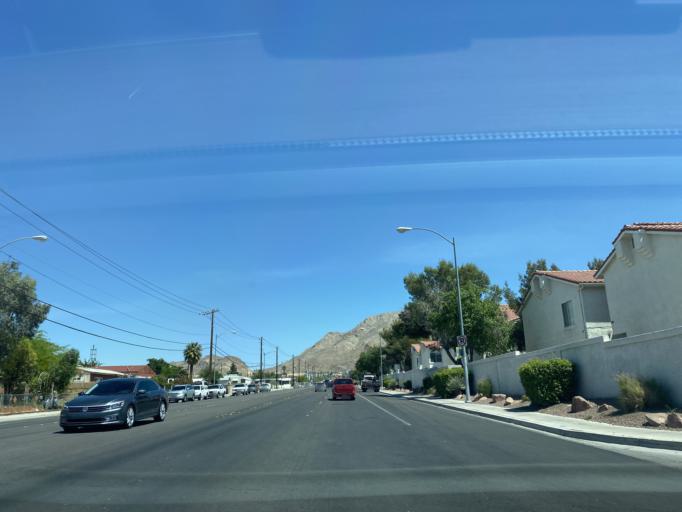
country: US
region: Nevada
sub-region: Clark County
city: Sunrise Manor
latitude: 36.1960
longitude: -115.0397
